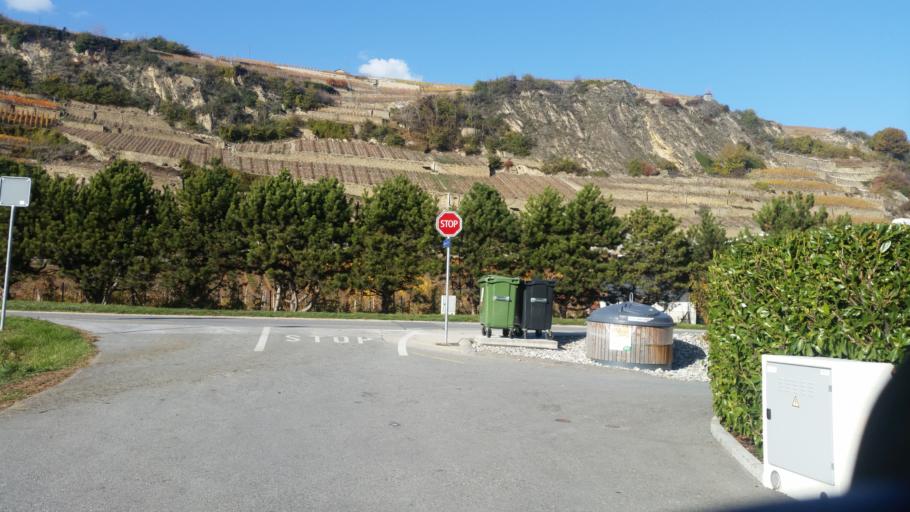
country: CH
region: Valais
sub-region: Sion District
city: Saint-Leonard
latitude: 46.2506
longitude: 7.4069
